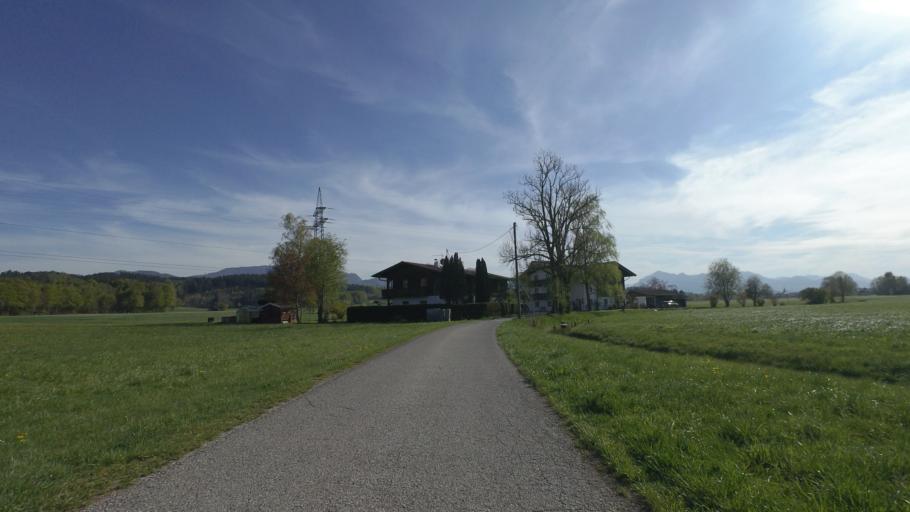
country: DE
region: Bavaria
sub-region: Upper Bavaria
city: Grabenstatt
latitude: 47.8504
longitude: 12.5607
